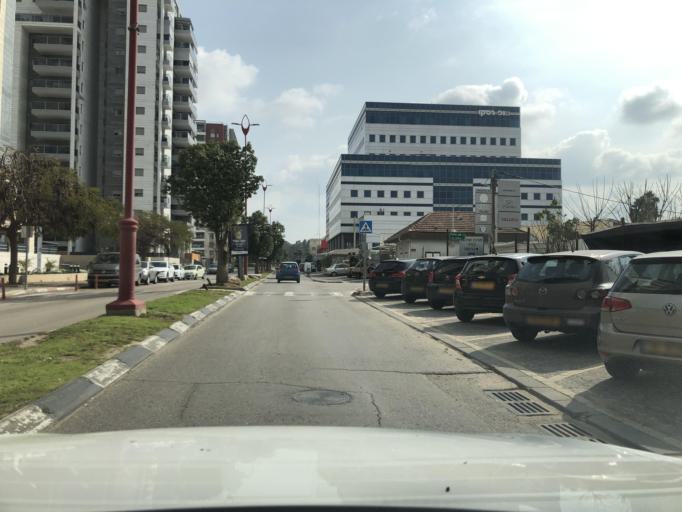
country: IL
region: Central District
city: Yehud
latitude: 32.0283
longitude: 34.8877
